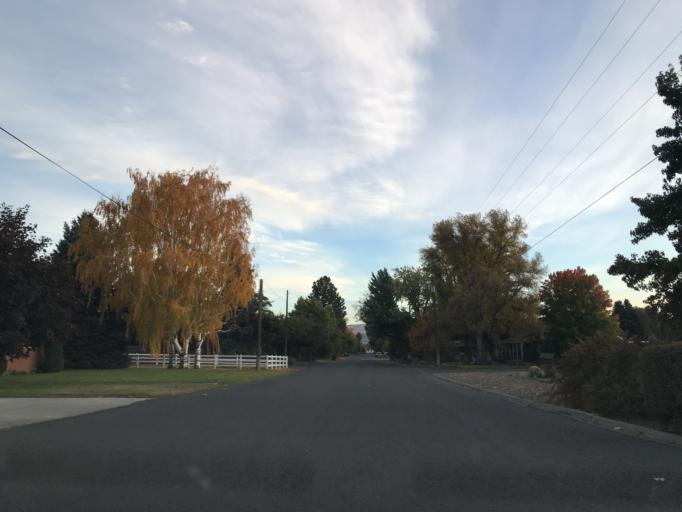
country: US
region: Washington
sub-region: Kittitas County
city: Ellensburg
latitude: 46.9912
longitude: -120.5331
